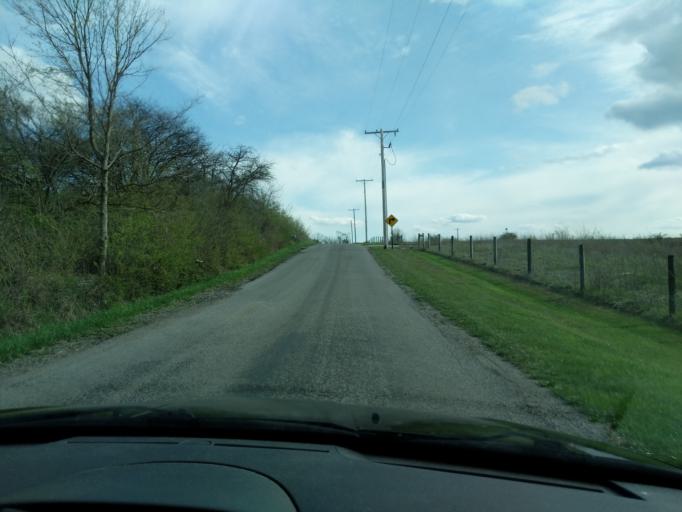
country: US
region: Ohio
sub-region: Champaign County
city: Urbana
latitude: 40.1383
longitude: -83.6502
